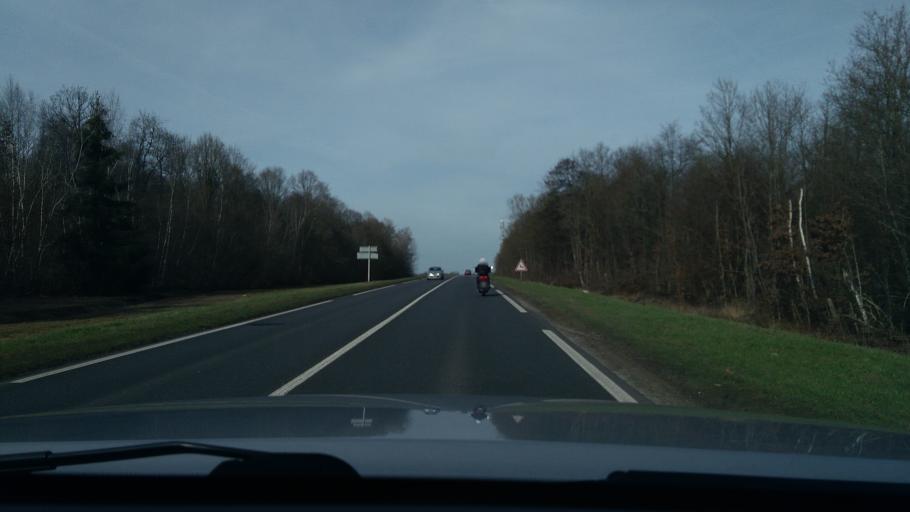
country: FR
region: Ile-de-France
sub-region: Departement de Seine-et-Marne
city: Chaumes-en-Brie
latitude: 48.6658
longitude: 2.8109
